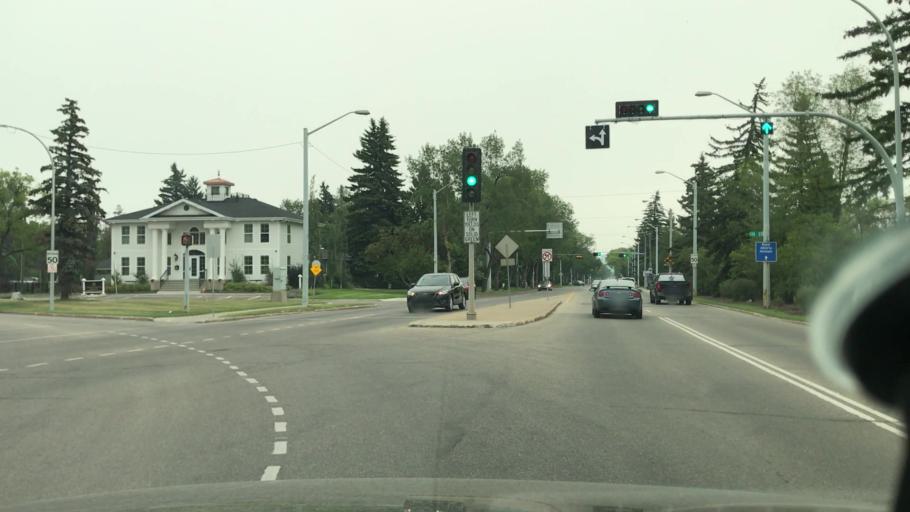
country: CA
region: Alberta
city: Edmonton
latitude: 53.5430
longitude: -113.5623
